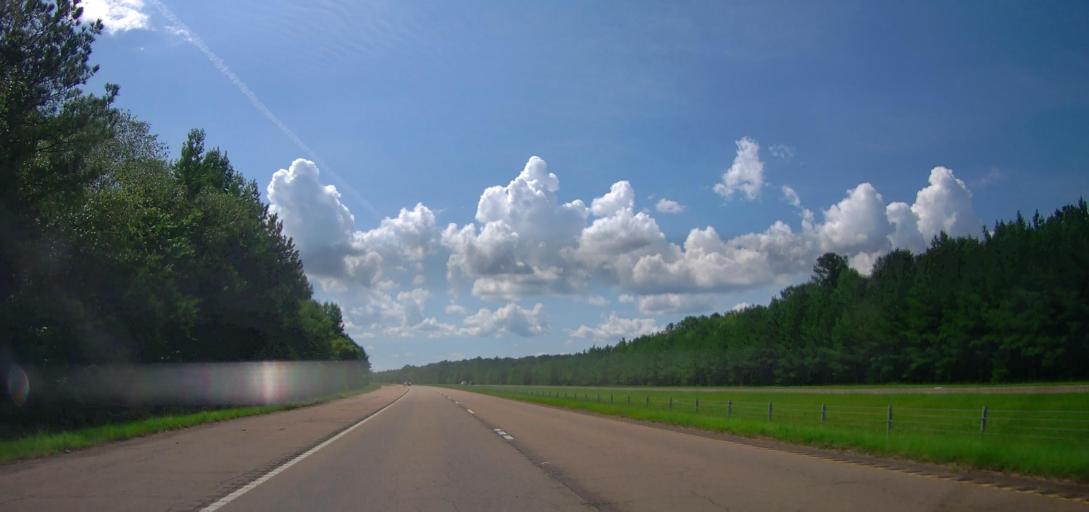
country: US
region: Mississippi
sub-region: Lowndes County
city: New Hope
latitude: 33.5059
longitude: -88.3159
